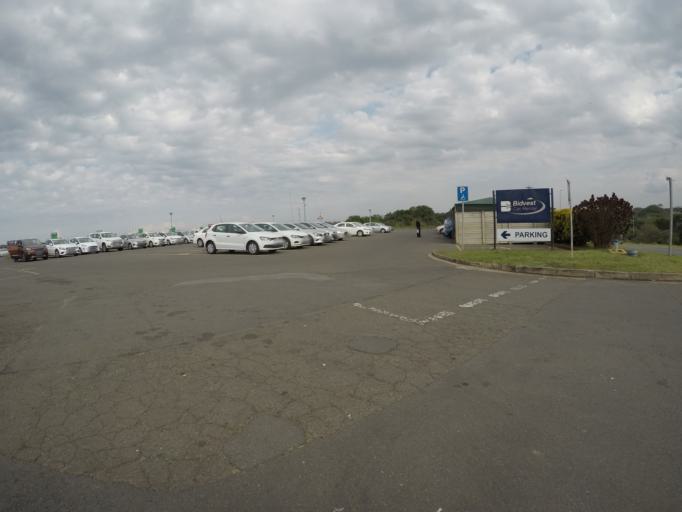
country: ZA
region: KwaZulu-Natal
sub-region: uThungulu District Municipality
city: Richards Bay
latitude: -28.7372
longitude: 32.0934
